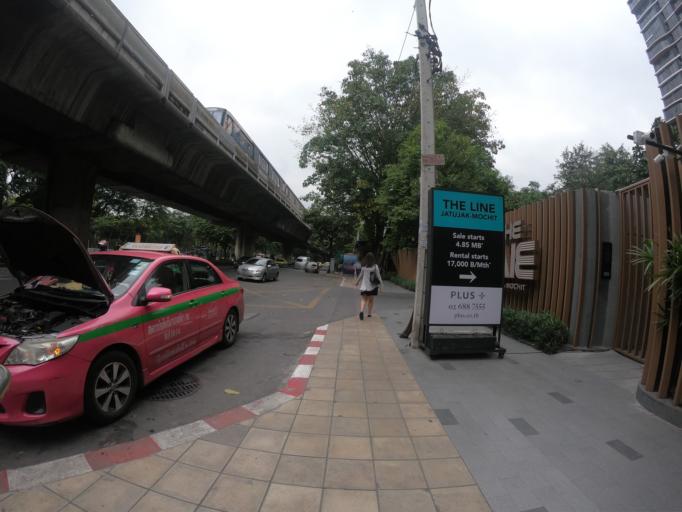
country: TH
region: Bangkok
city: Chatuchak
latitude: 13.8357
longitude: 100.5523
